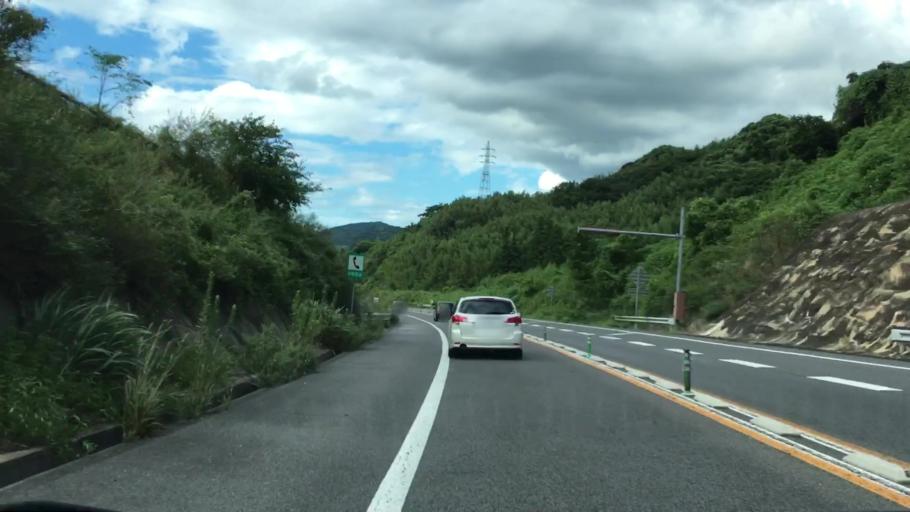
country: JP
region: Saga Prefecture
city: Karatsu
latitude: 33.4315
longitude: 130.0483
